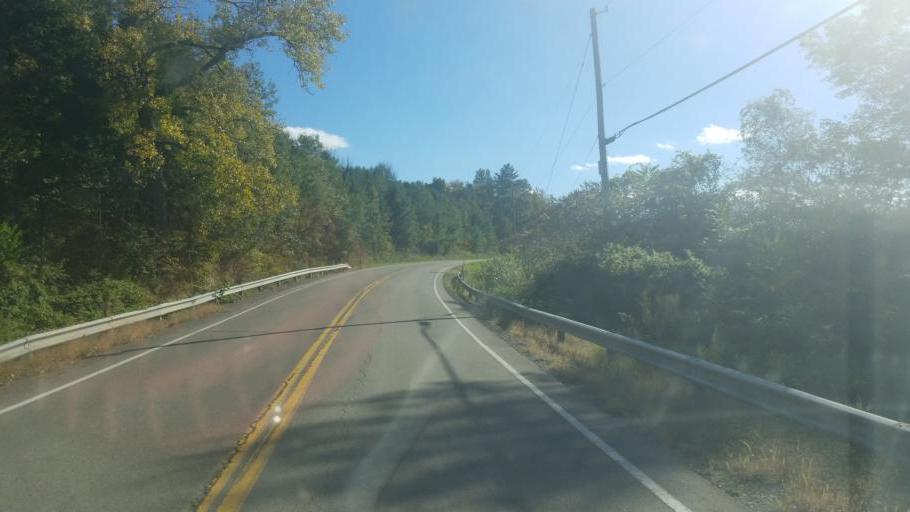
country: US
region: New York
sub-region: Allegany County
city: Friendship
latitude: 42.2909
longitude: -78.1188
